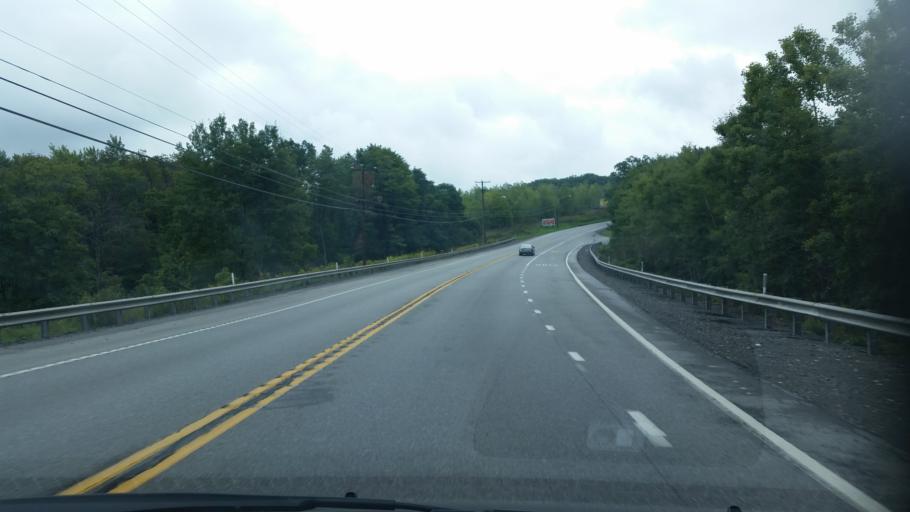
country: US
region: Pennsylvania
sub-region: Clearfield County
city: Shiloh
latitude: 40.9986
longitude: -78.3200
